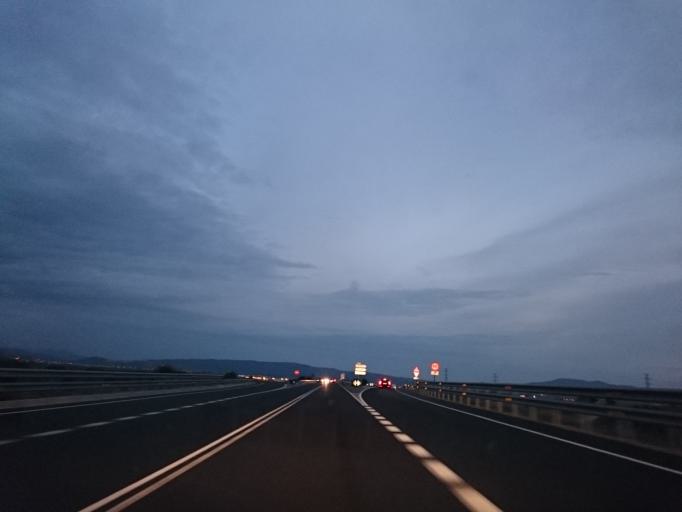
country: ES
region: Catalonia
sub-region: Provincia de Barcelona
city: La Granada
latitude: 41.3682
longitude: 1.7135
